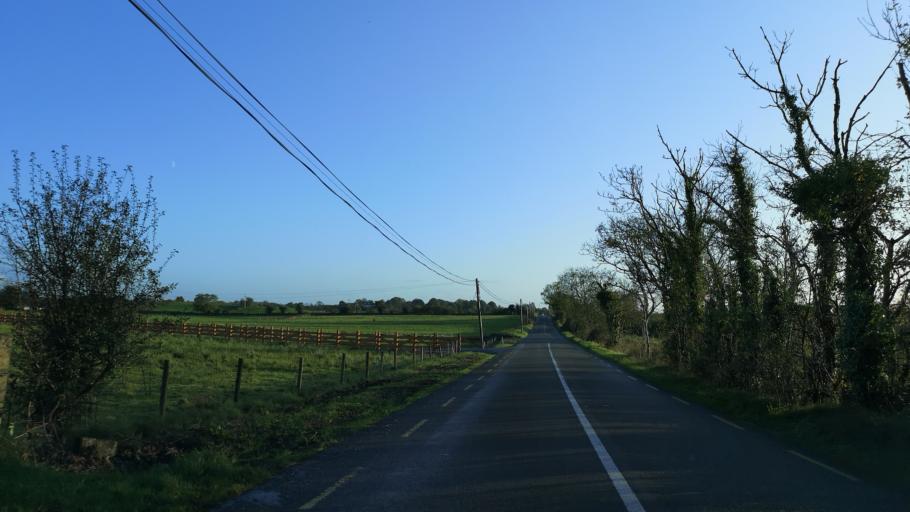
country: IE
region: Connaught
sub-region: Roscommon
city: Castlerea
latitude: 53.7098
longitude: -8.5643
